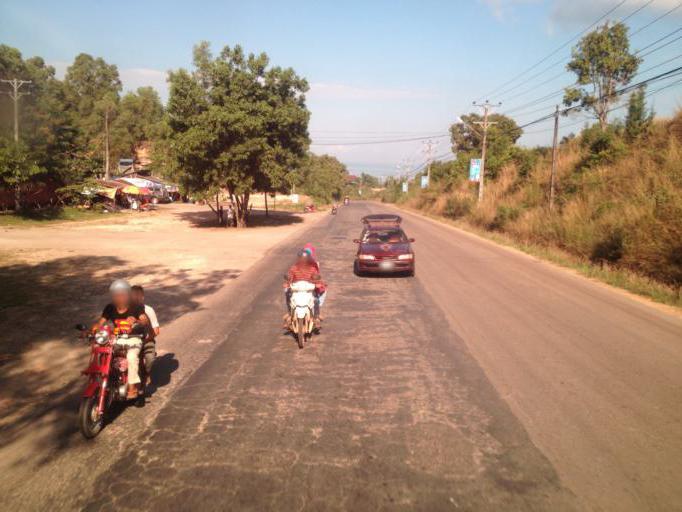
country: KH
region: Preah Sihanouk
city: Sihanoukville
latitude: 10.6395
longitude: 103.5302
